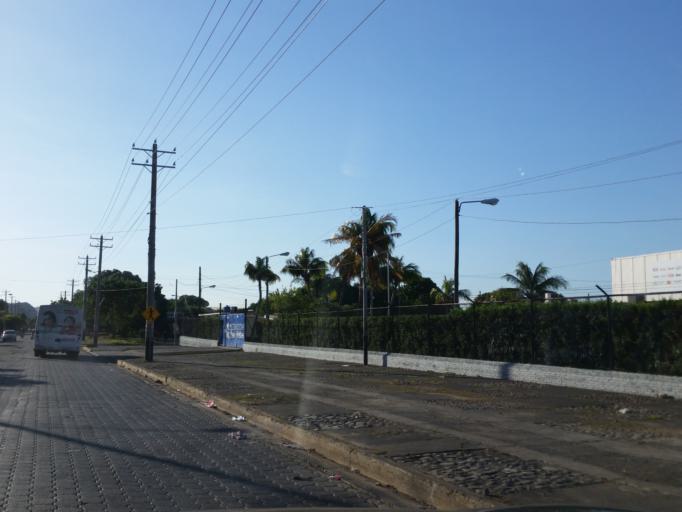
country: NI
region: Managua
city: Ciudad Sandino
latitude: 12.1581
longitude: -86.3008
